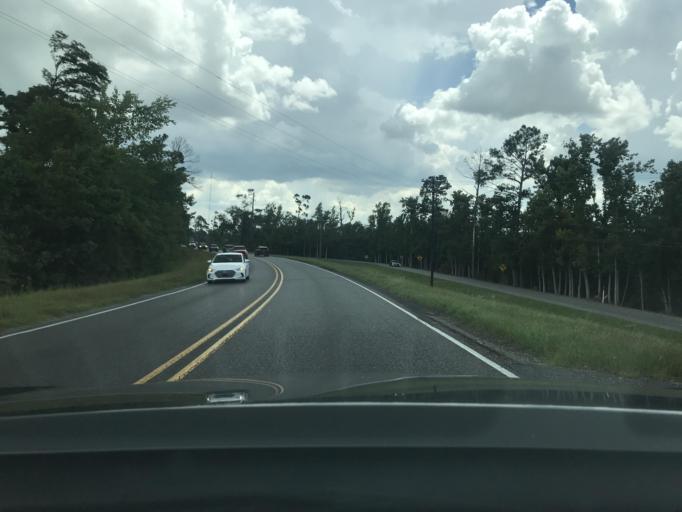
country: US
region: Louisiana
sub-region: Calcasieu Parish
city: Westlake
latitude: 30.2960
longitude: -93.2495
